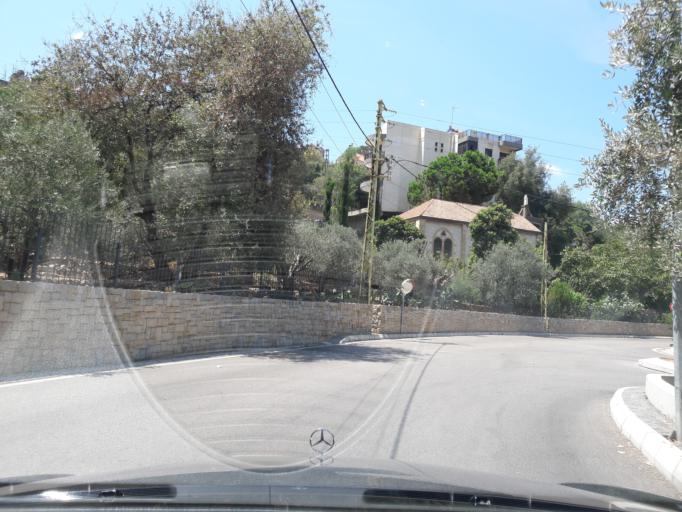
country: LB
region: Mont-Liban
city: Djounie
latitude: 33.9197
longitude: 35.6391
